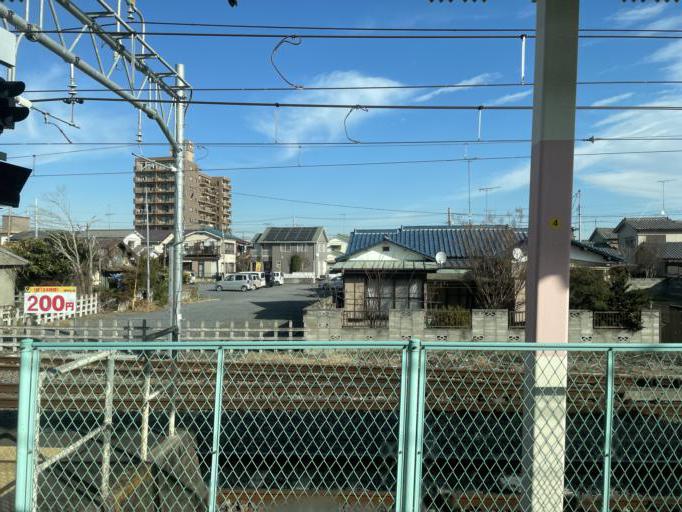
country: JP
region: Saitama
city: Fukiage-fujimi
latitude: 36.1023
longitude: 139.4552
